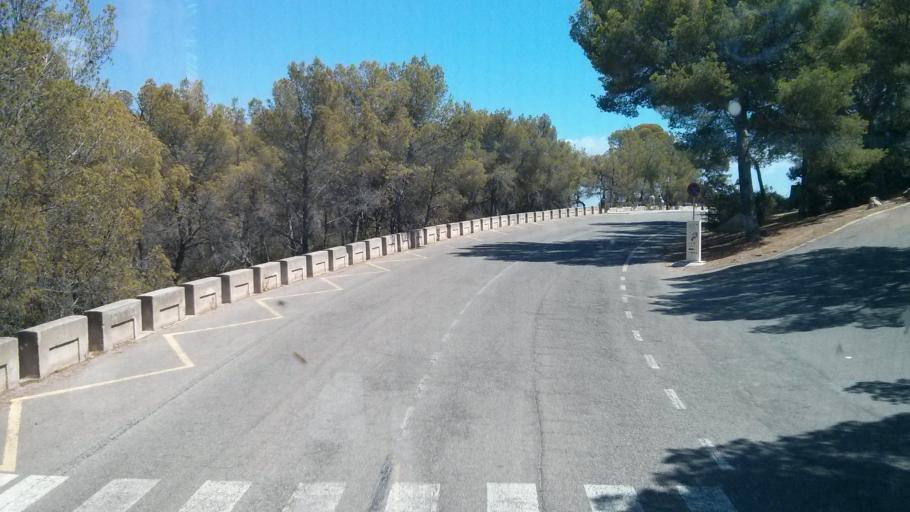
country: ES
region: Balearic Islands
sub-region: Illes Balears
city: Palma
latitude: 39.5649
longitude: 2.6188
